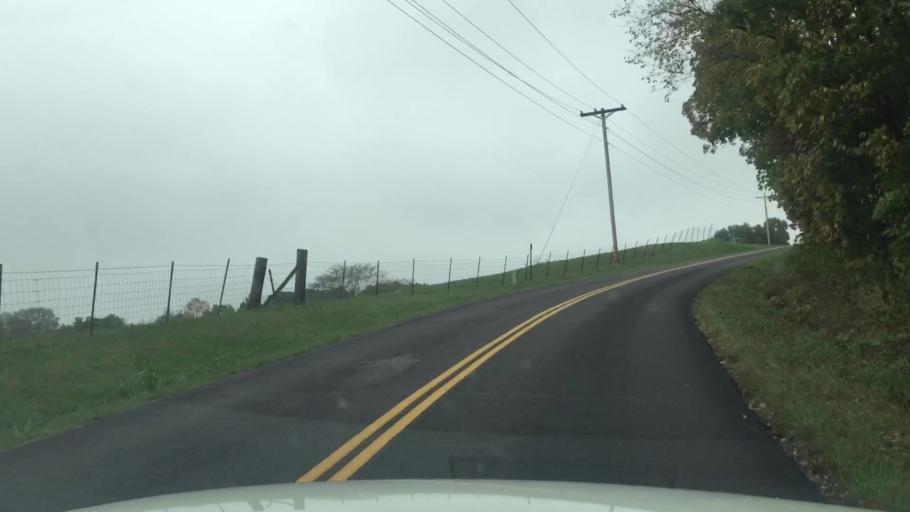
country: US
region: Missouri
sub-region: Boone County
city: Ashland
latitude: 38.8214
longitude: -92.3479
